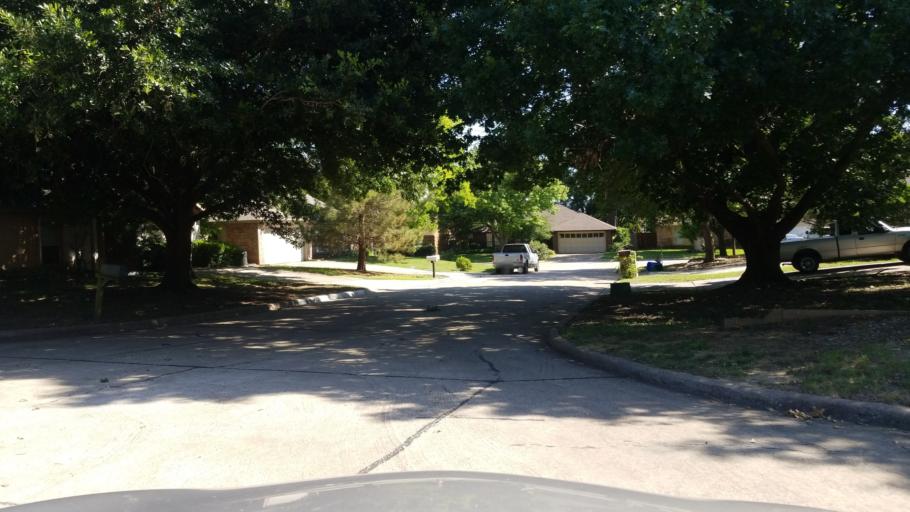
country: US
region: Texas
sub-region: Dallas County
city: Grand Prairie
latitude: 32.6799
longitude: -97.0162
